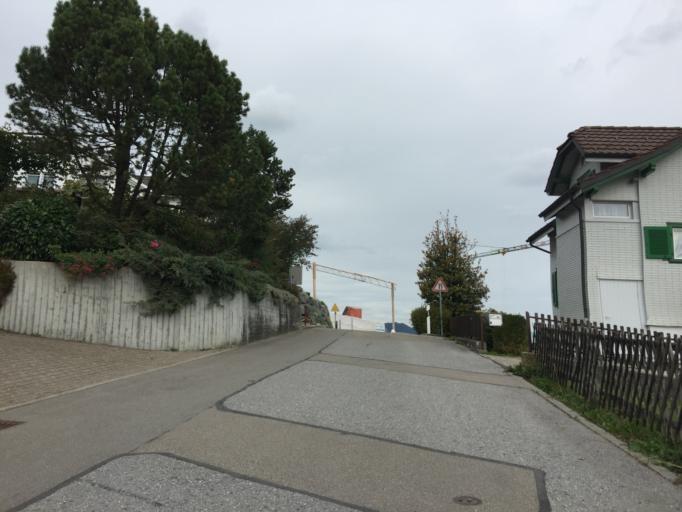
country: CH
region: Saint Gallen
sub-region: Wahlkreis Wil
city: Oberuzwil
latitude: 47.4360
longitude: 9.1274
